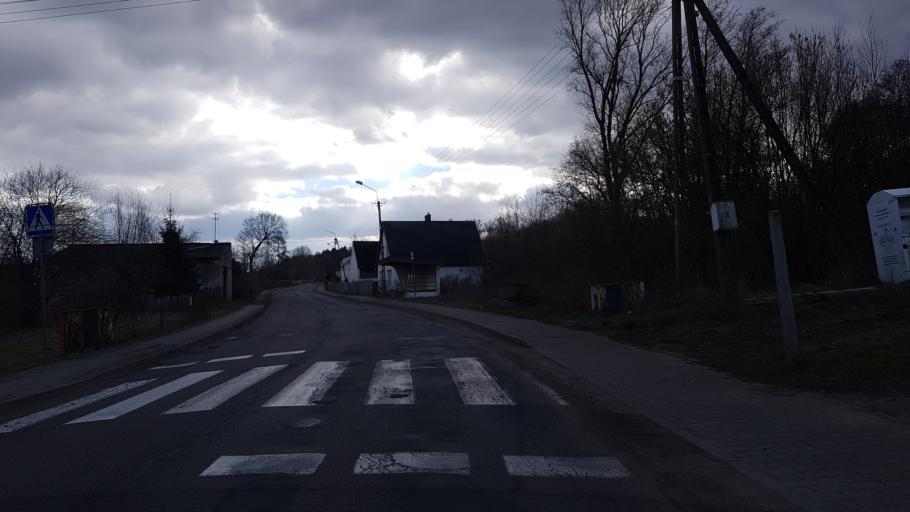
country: PL
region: West Pomeranian Voivodeship
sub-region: Powiat koszalinski
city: Bobolice
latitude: 53.9782
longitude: 16.5391
